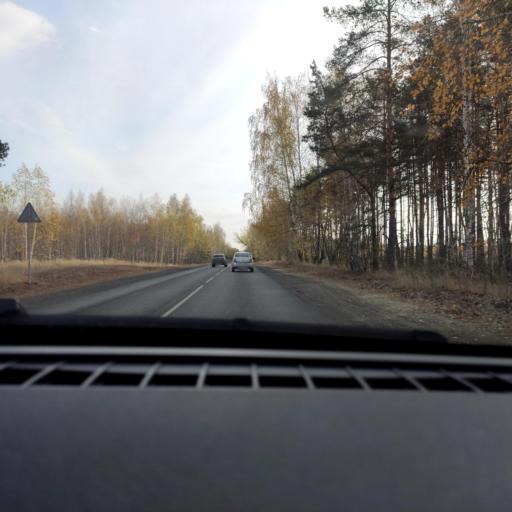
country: RU
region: Voronezj
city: Maslovka
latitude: 51.5809
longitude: 39.2814
